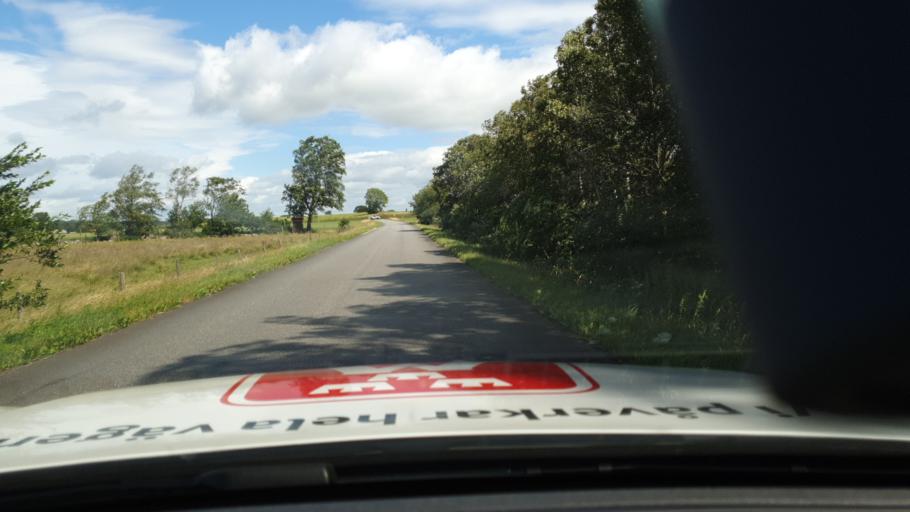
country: SE
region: Vaestra Goetaland
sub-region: Falkopings Kommun
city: Falkoeping
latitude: 58.1469
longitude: 13.6053
